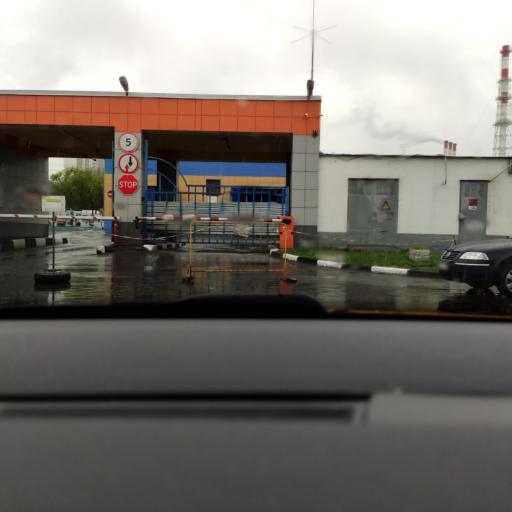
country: RU
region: Moscow
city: Strogino
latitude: 55.8387
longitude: 37.4244
